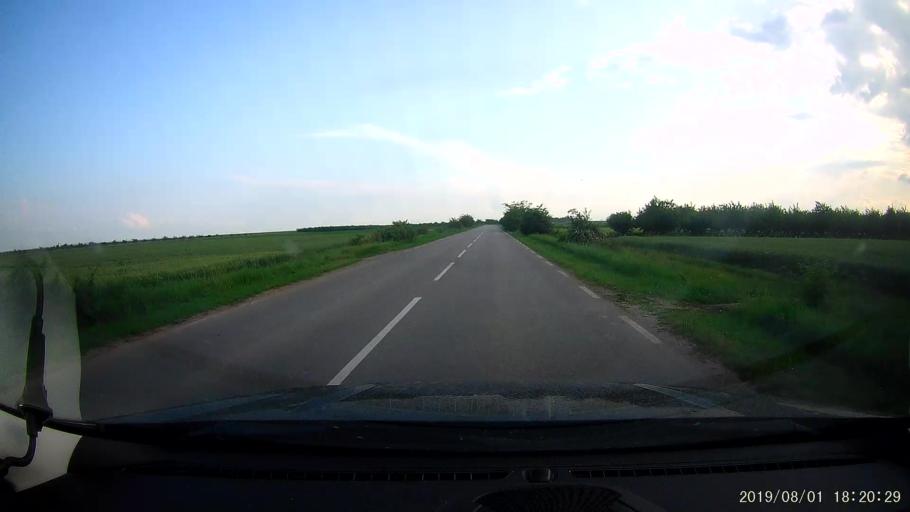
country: BG
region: Shumen
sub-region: Obshtina Kaolinovo
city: Kaolinovo
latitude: 43.6702
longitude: 27.0880
